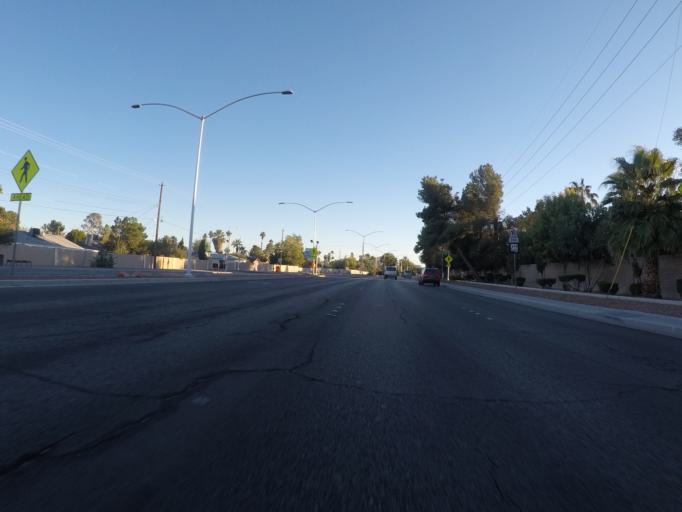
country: US
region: Nevada
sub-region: Clark County
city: Las Vegas
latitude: 36.1718
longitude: -115.1728
